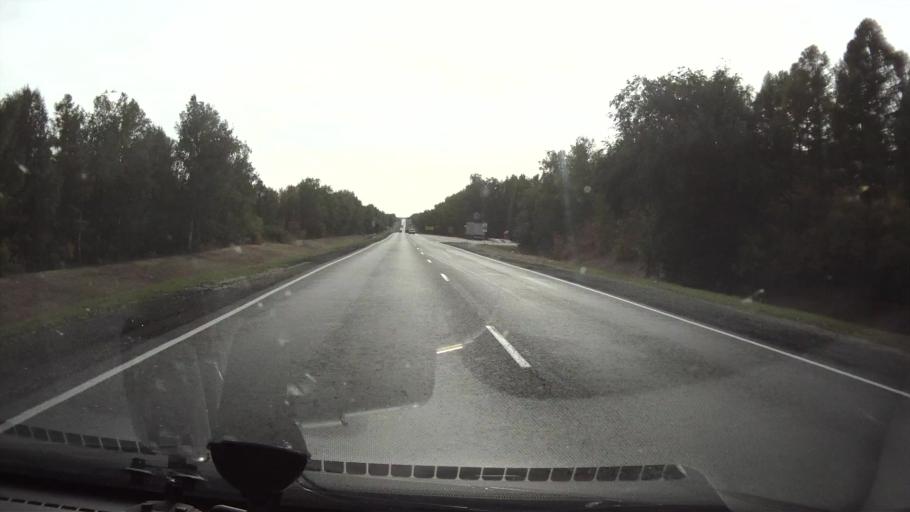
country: RU
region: Saratov
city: Sennoy
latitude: 52.1299
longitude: 46.8601
